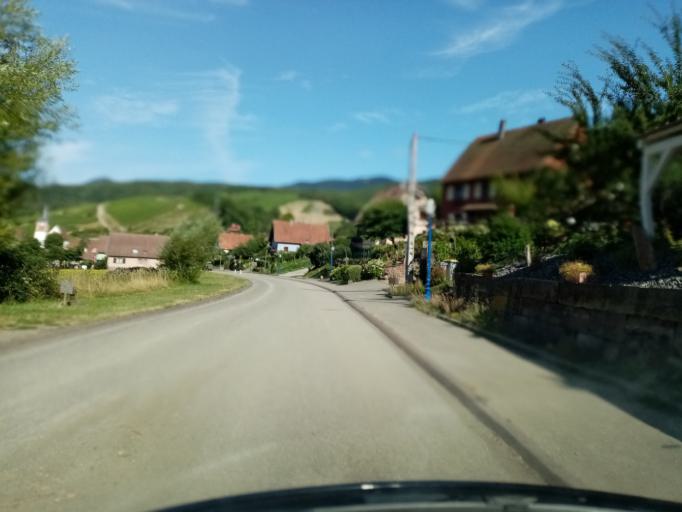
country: FR
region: Alsace
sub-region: Departement du Bas-Rhin
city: Ville
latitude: 48.3555
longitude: 7.3230
